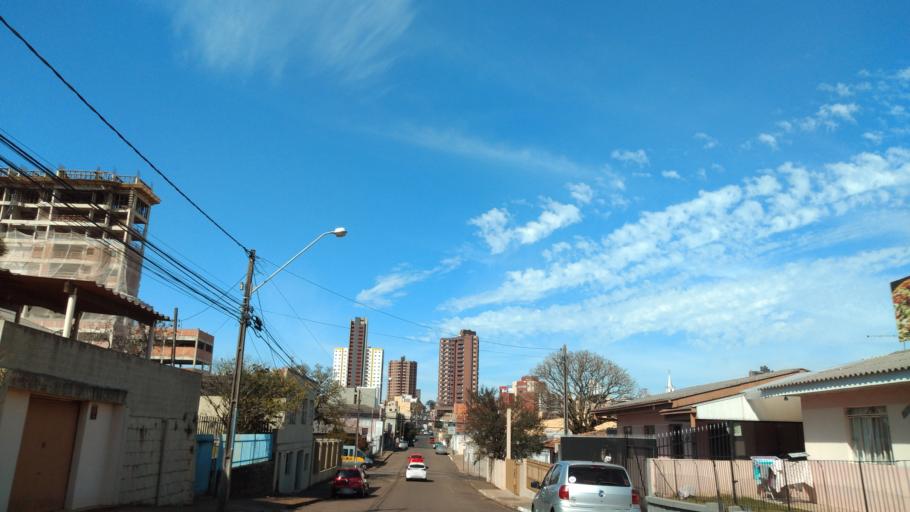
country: BR
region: Parana
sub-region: Guarapuava
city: Guarapuava
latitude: -25.3884
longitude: -51.4682
